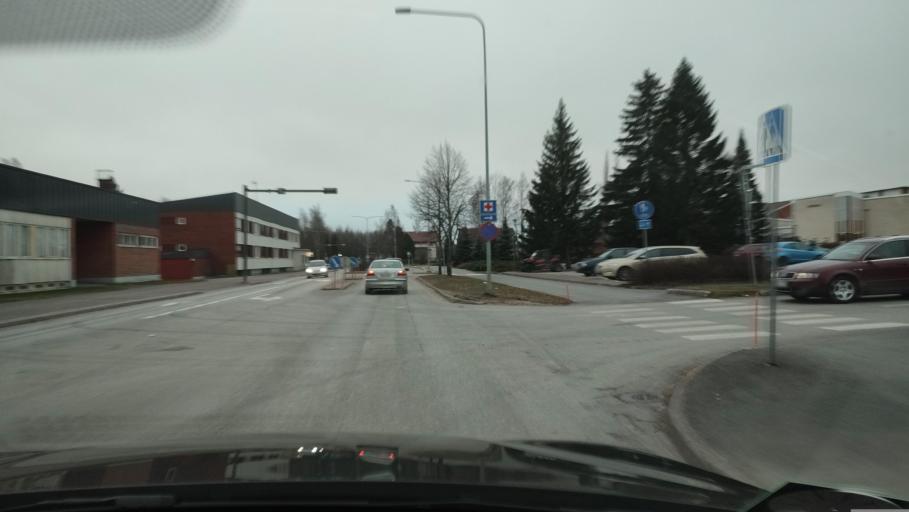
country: FI
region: Southern Ostrobothnia
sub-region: Suupohja
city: Kauhajoki
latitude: 62.4233
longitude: 22.1757
